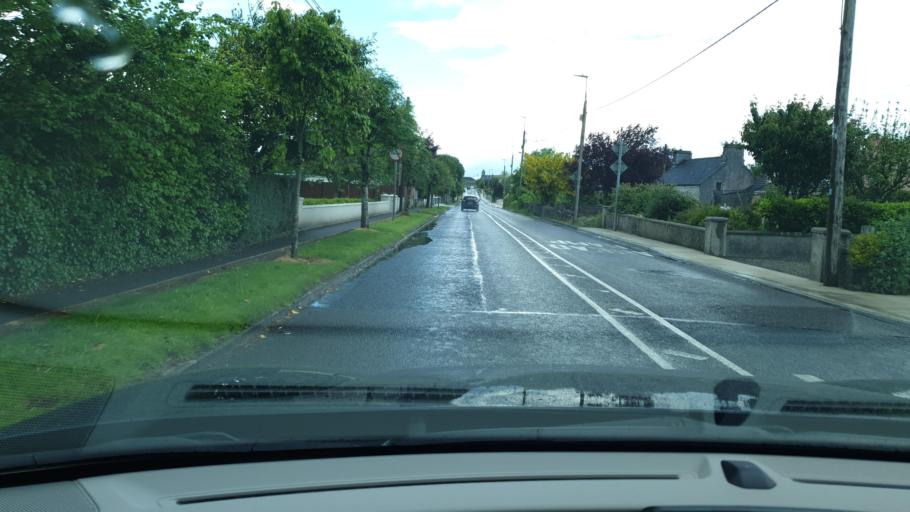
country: IE
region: Connaught
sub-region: County Galway
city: Ballinasloe
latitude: 53.3243
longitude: -8.1945
